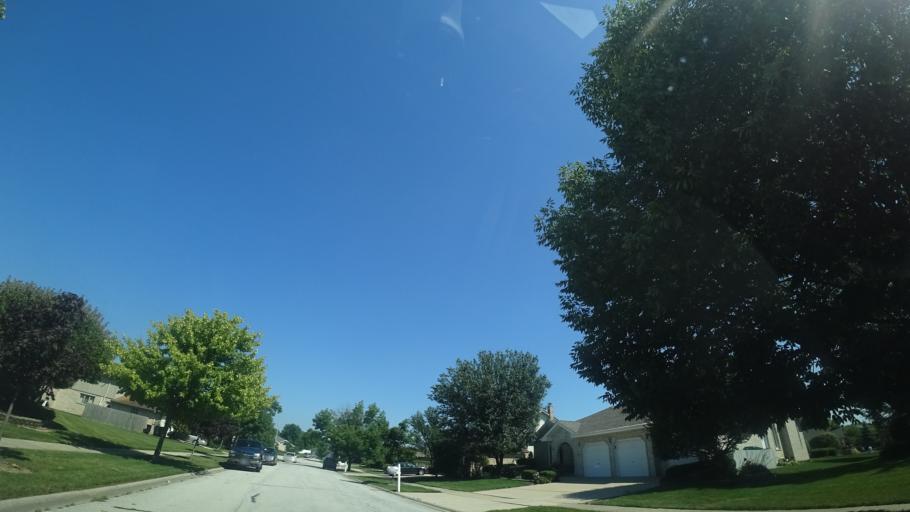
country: US
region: Illinois
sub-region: Will County
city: Homer Glen
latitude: 41.5719
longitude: -87.9087
